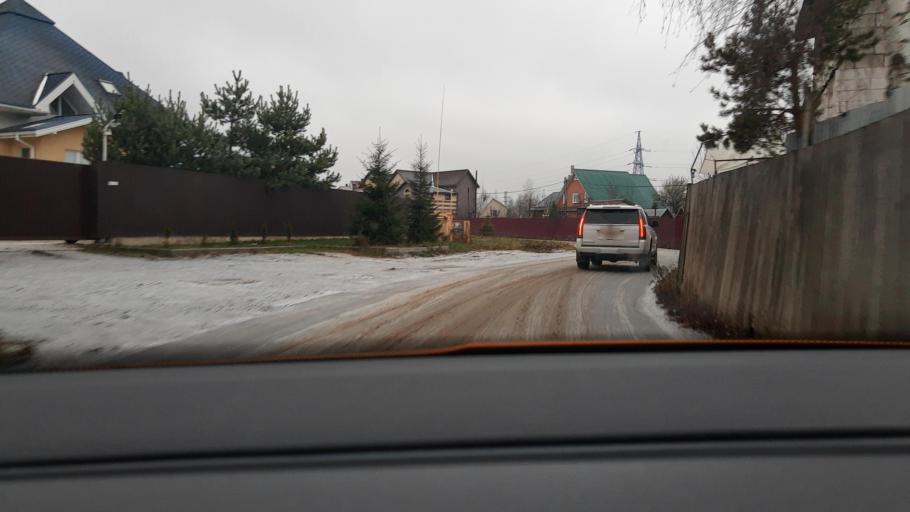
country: RU
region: Moscow
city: Severnyy
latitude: 55.9570
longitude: 37.5589
